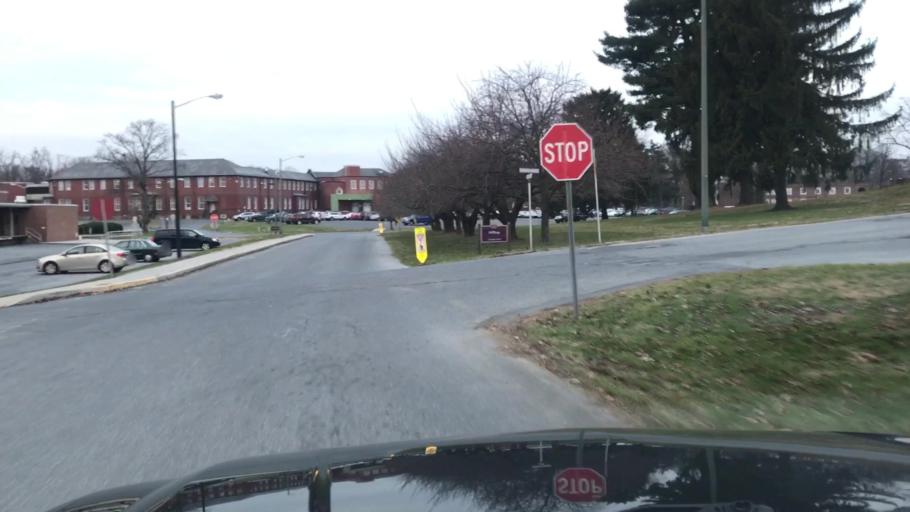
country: US
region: Pennsylvania
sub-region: Dauphin County
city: Harrisburg
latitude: 40.2851
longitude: -76.8703
